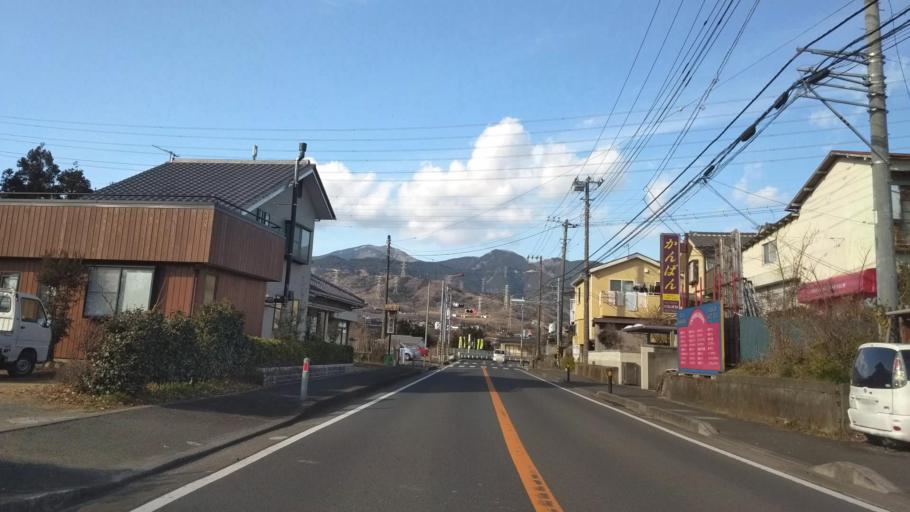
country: JP
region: Kanagawa
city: Hadano
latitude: 35.3869
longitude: 139.2362
